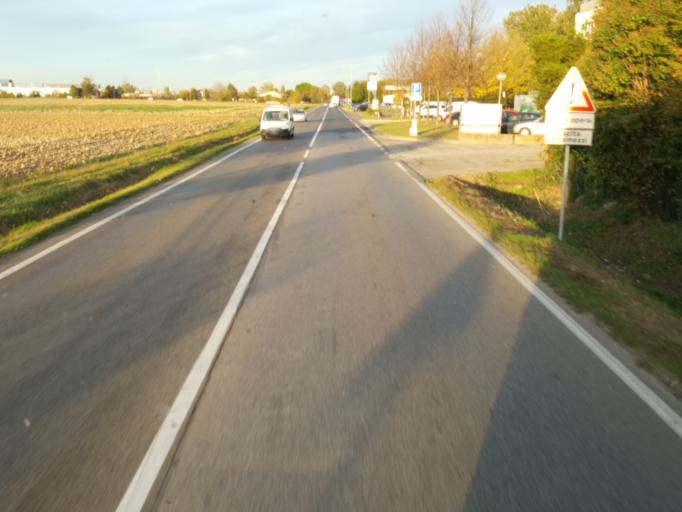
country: IT
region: Emilia-Romagna
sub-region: Provincia di Ravenna
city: Faenza
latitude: 44.3149
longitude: 11.8920
